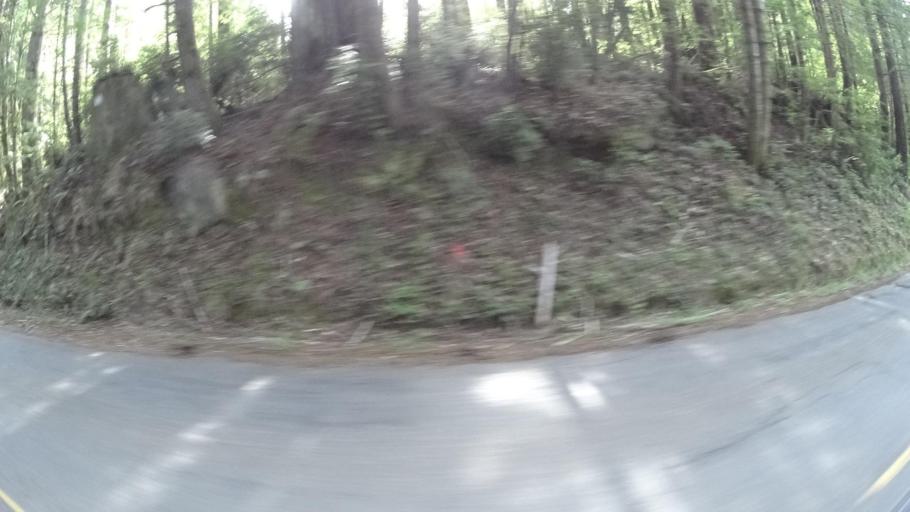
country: US
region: California
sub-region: Humboldt County
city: Bayside
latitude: 40.7608
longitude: -124.0005
